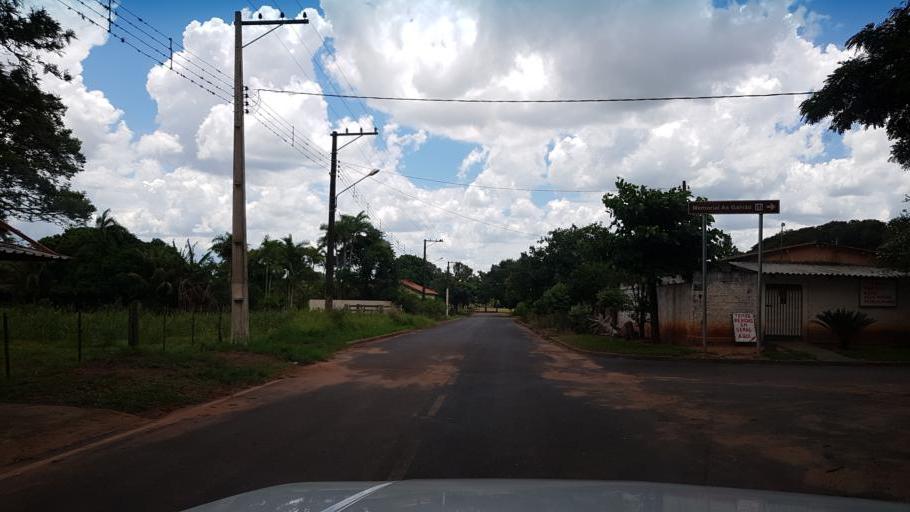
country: BR
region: Sao Paulo
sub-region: Paraguacu Paulista
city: Paraguacu Paulista
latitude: -22.3529
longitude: -50.6242
